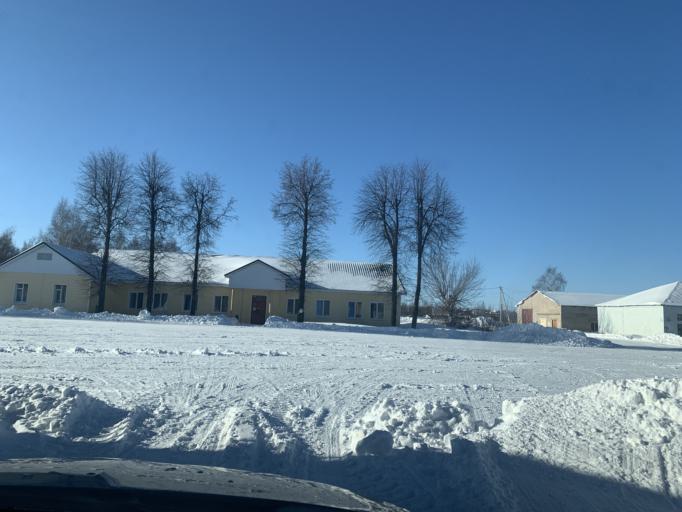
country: RU
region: Jaroslavl
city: Tunoshna
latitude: 57.6595
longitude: 40.0711
